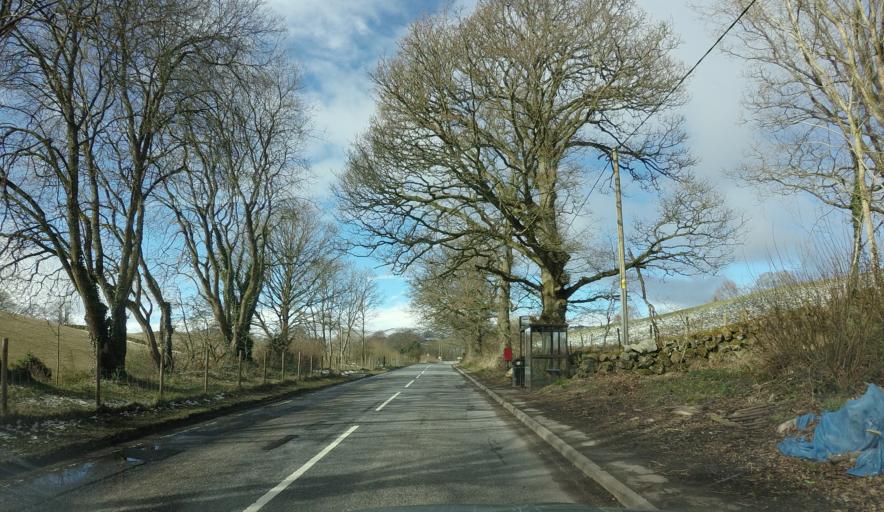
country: GB
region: Scotland
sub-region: Perth and Kinross
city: Bankfoot
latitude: 56.5135
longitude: -3.5290
